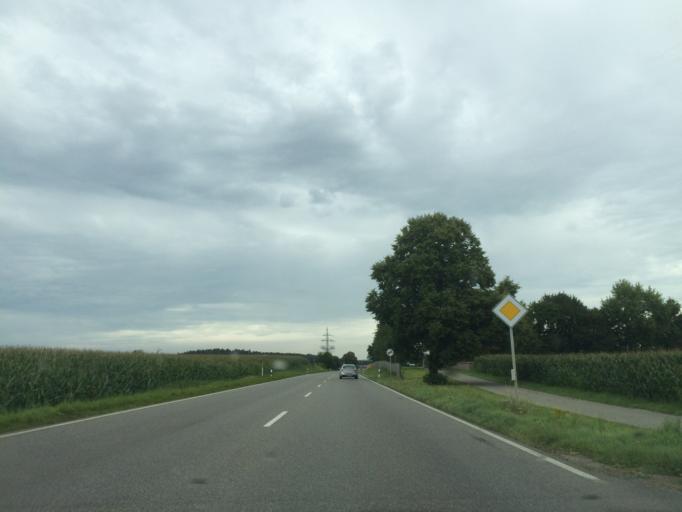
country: DE
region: Baden-Wuerttemberg
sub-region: Tuebingen Region
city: Horgenzell
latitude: 47.7650
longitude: 9.5470
